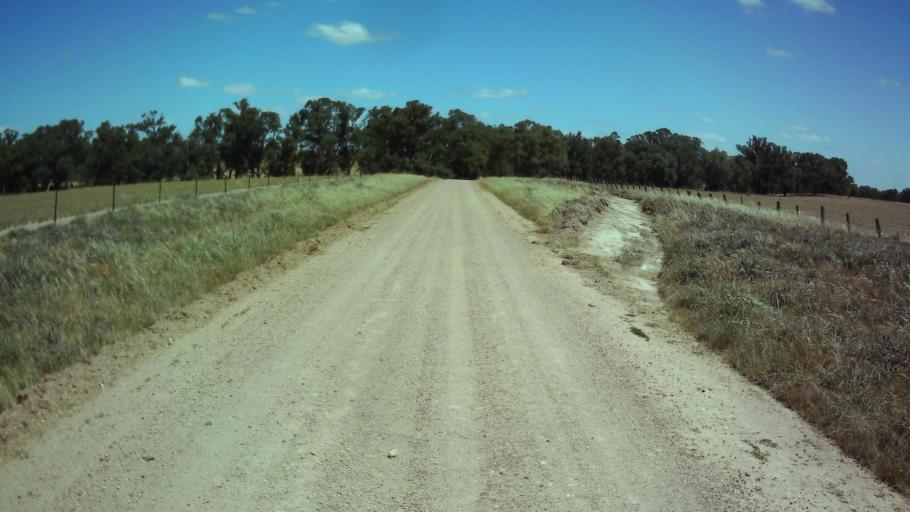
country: AU
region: New South Wales
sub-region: Weddin
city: Grenfell
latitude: -33.9309
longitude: 148.3345
